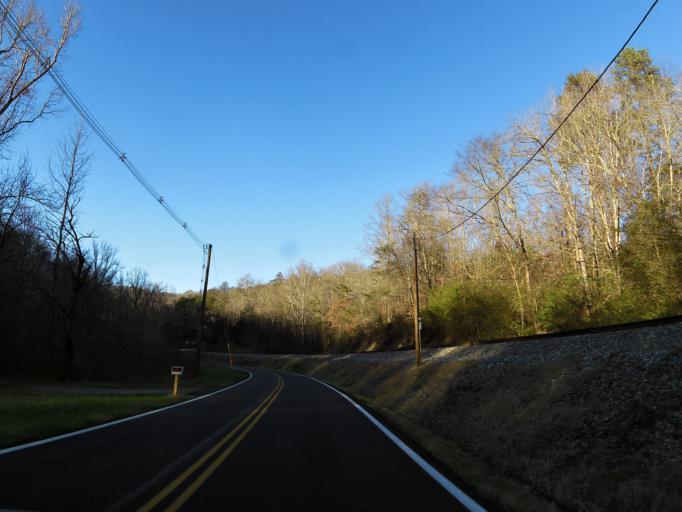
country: US
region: Tennessee
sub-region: Anderson County
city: Oak Ridge
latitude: 36.0710
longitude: -84.2467
